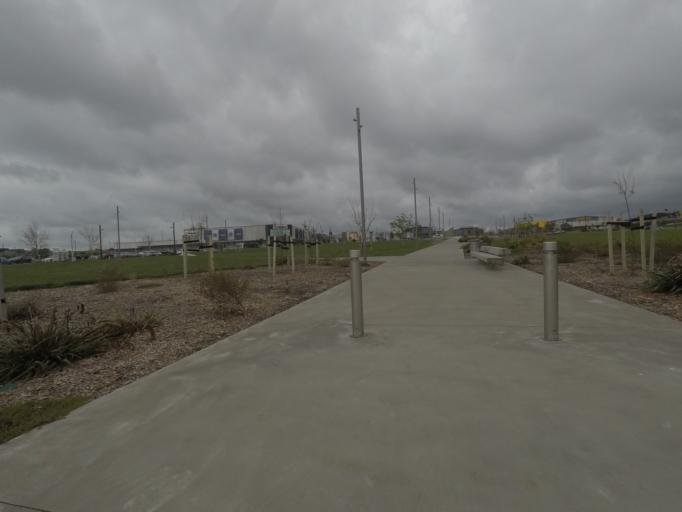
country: NZ
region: Auckland
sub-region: Auckland
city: Rosebank
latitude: -36.8156
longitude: 174.6086
